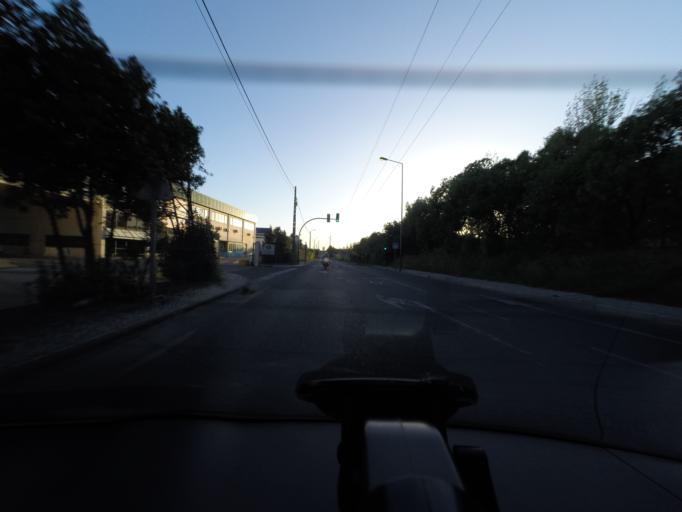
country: PT
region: Lisbon
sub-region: Sintra
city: Sintra
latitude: 38.7593
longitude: -9.3748
